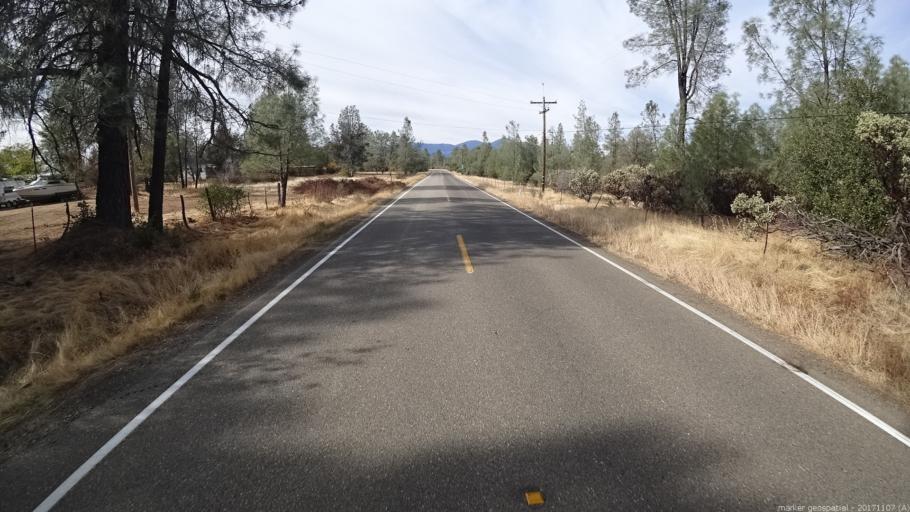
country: US
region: California
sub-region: Shasta County
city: Shasta
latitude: 40.4750
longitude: -122.4897
